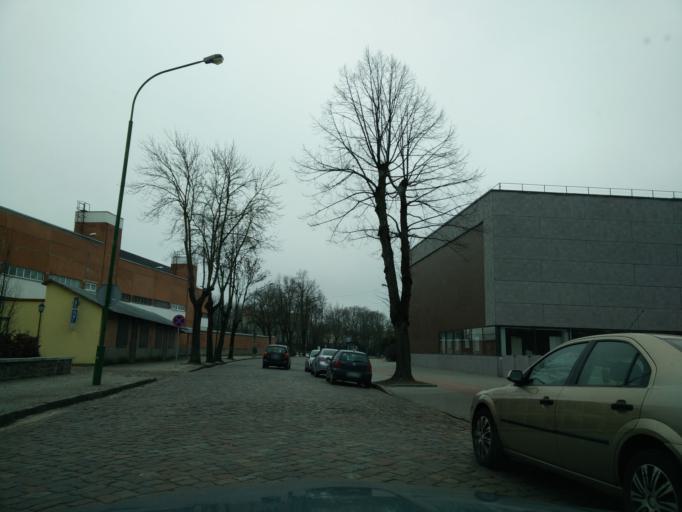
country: LT
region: Klaipedos apskritis
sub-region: Klaipeda
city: Klaipeda
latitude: 55.7081
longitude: 21.1420
